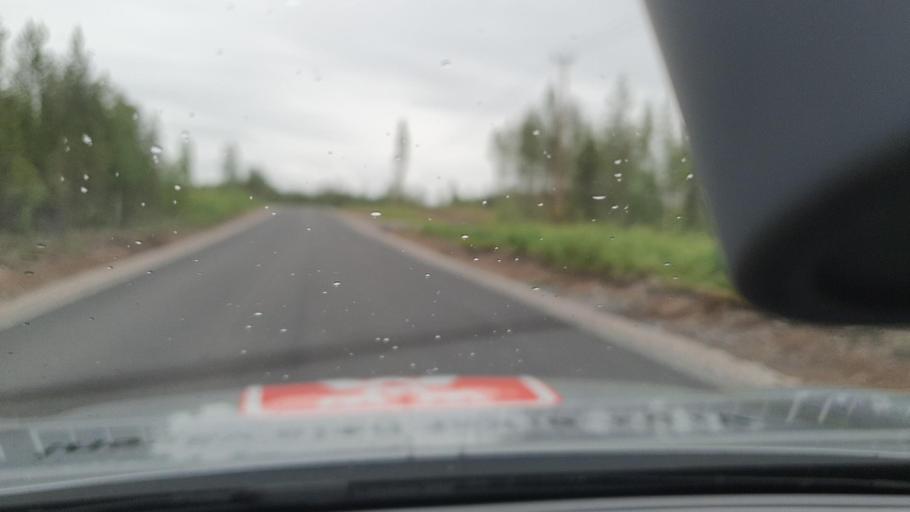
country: SE
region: Norrbotten
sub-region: Overkalix Kommun
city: OEverkalix
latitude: 66.6588
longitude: 23.2219
